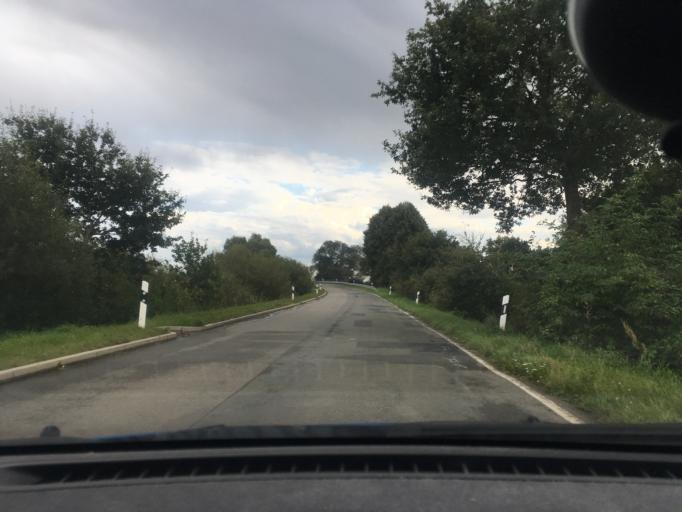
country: DE
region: Lower Saxony
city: Neu Darchau
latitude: 53.3394
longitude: 10.8601
